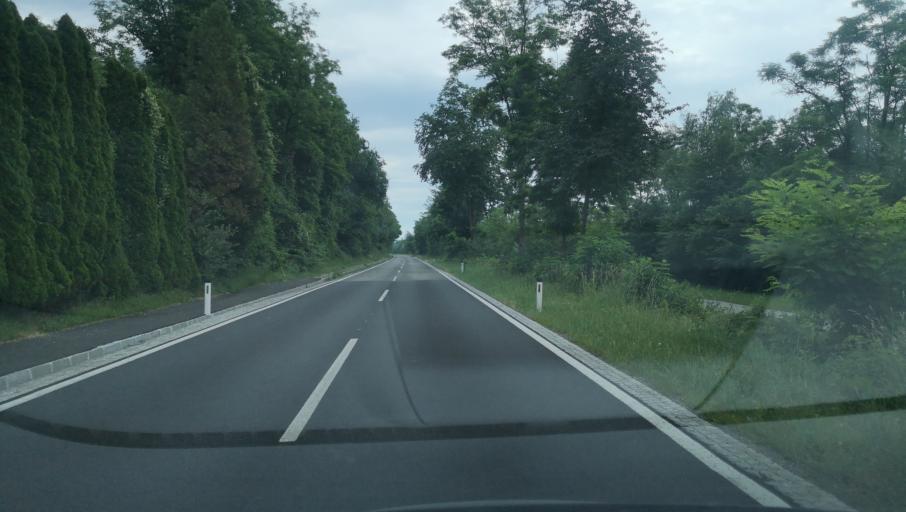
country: AT
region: Lower Austria
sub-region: Politischer Bezirk Melk
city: Leiben
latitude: 48.2267
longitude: 15.2659
